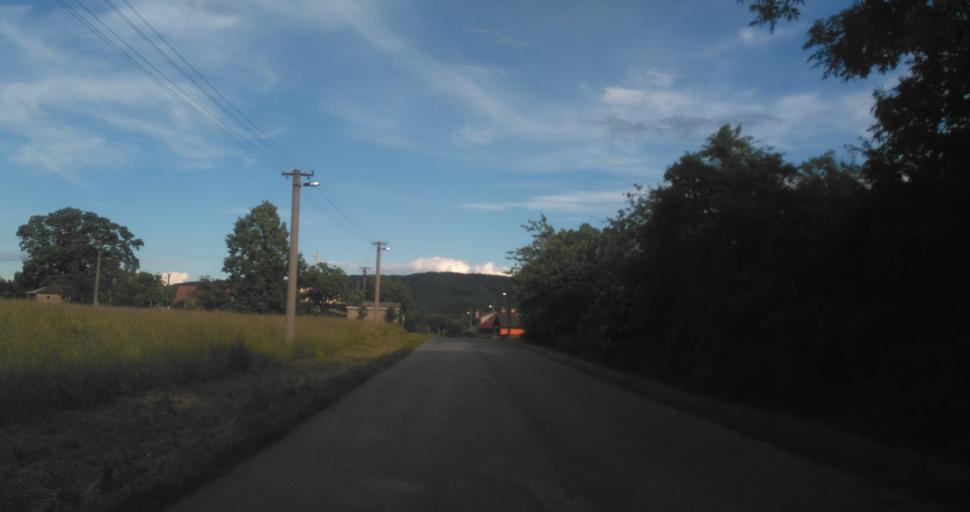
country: CZ
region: Central Bohemia
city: Roztoky
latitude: 49.9796
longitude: 13.8904
